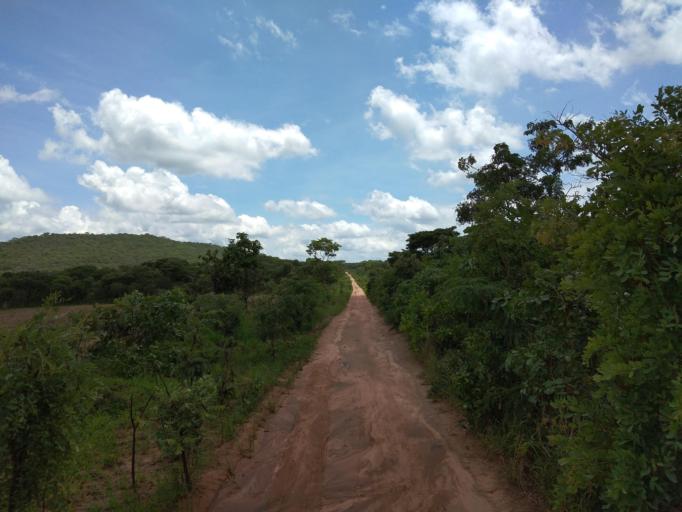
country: ZM
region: Central
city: Mkushi
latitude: -13.9158
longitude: 29.8663
